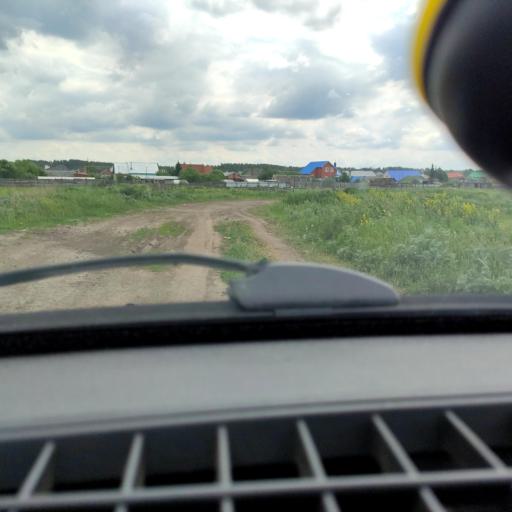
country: RU
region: Samara
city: Povolzhskiy
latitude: 53.6492
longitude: 49.6973
